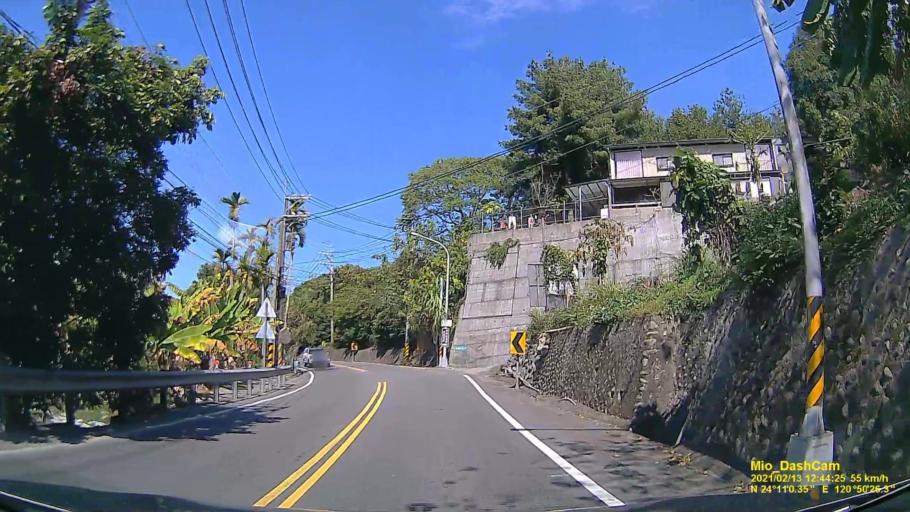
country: TW
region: Taiwan
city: Fengyuan
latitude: 24.1834
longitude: 120.8406
